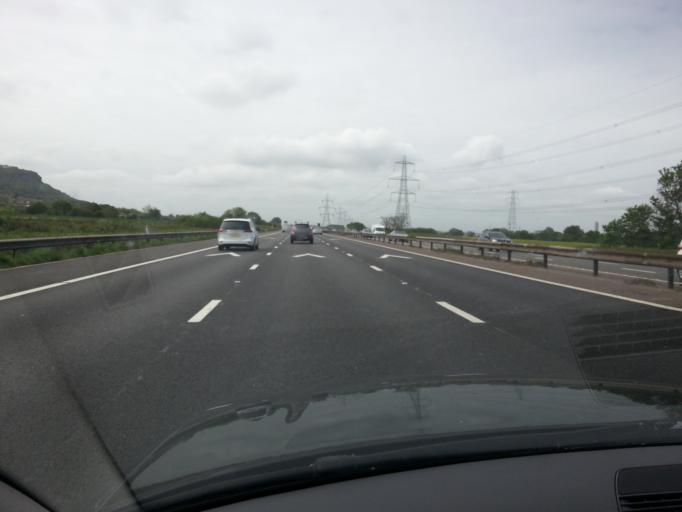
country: GB
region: England
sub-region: Cheshire West and Chester
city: Helsby
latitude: 53.2882
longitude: -2.7510
